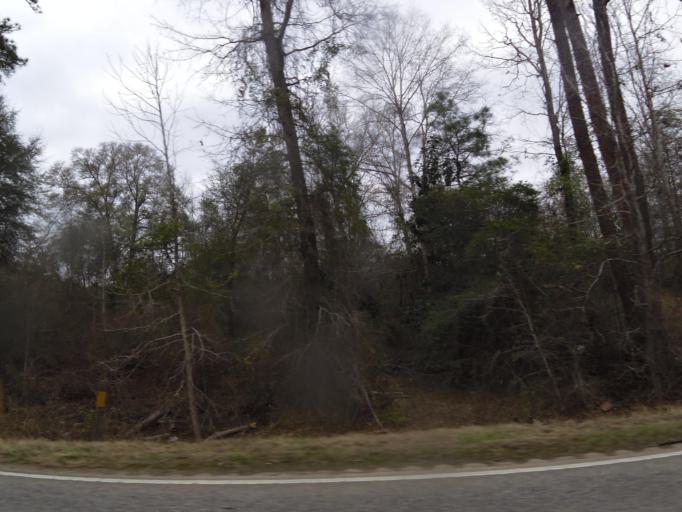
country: US
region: Alabama
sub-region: Barbour County
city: Eufaula
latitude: 31.9349
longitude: -85.1669
